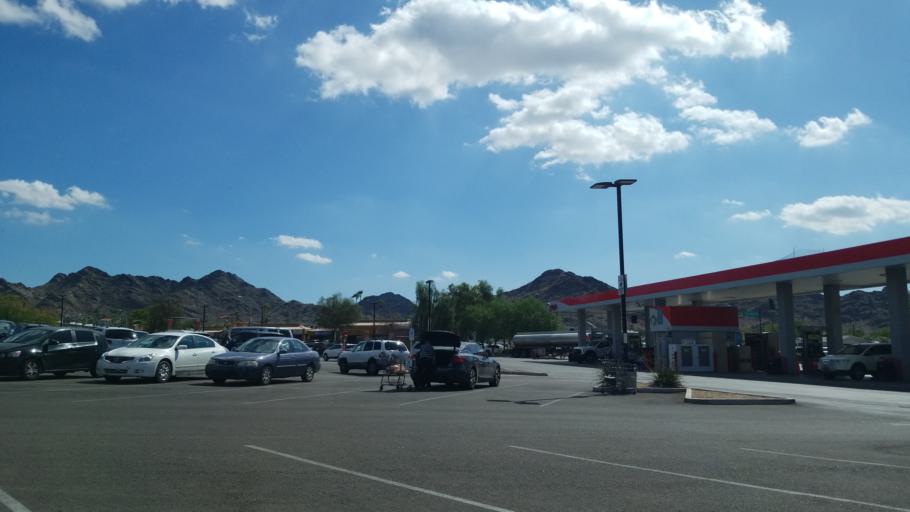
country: US
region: Arizona
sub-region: Maricopa County
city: Phoenix
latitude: 33.5719
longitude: -112.0614
